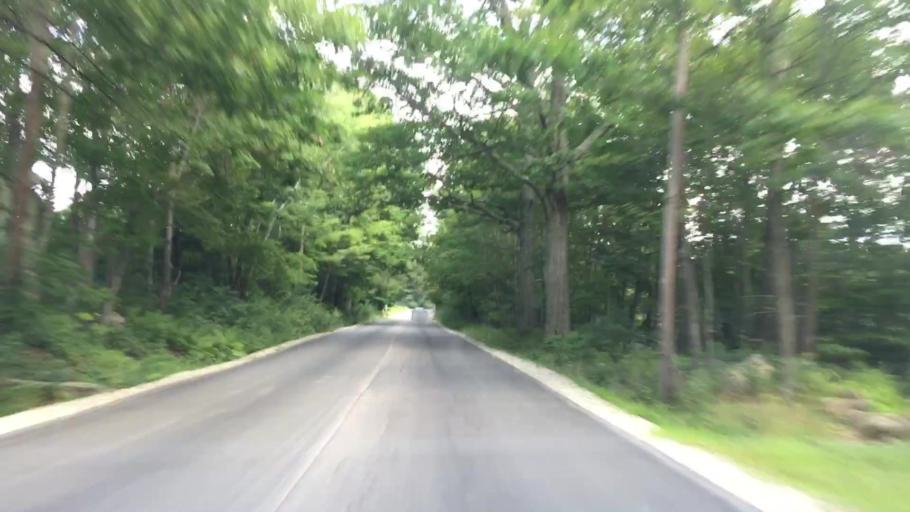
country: US
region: New Hampshire
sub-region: Belknap County
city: Sanbornton
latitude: 43.5050
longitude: -71.6040
